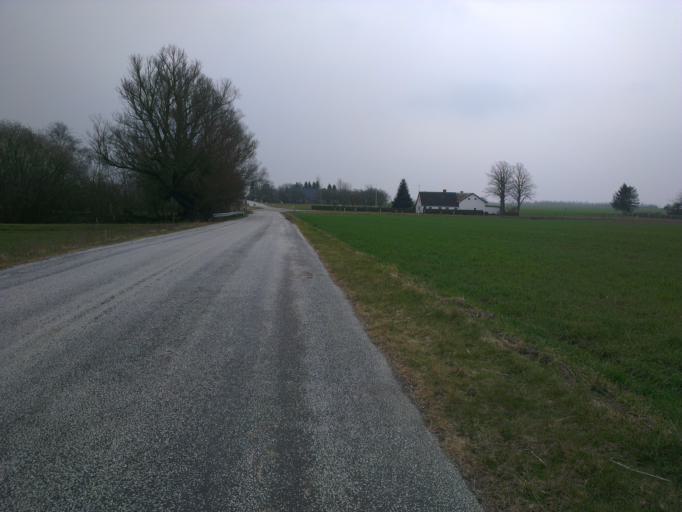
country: DK
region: Capital Region
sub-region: Egedal Kommune
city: Olstykke
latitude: 55.8067
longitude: 12.1092
